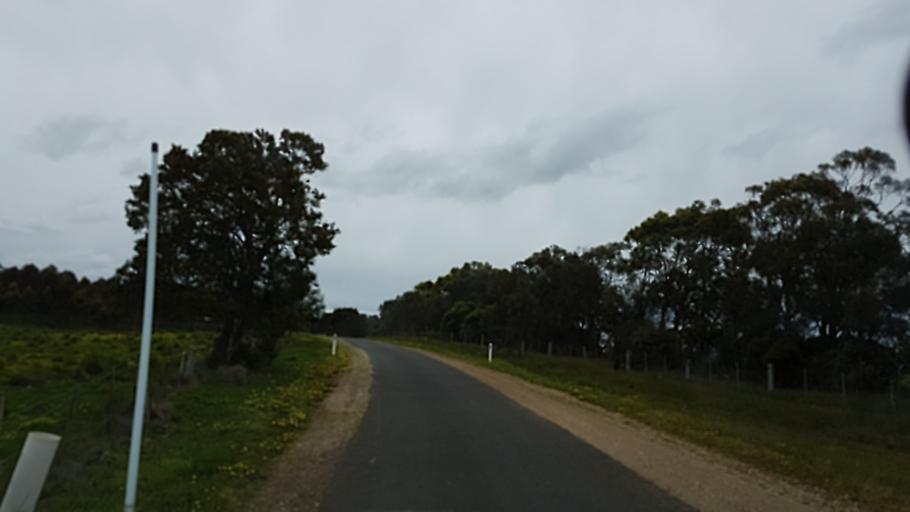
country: AU
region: Victoria
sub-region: Moorabool
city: Bacchus Marsh
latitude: -37.7401
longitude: 144.1590
